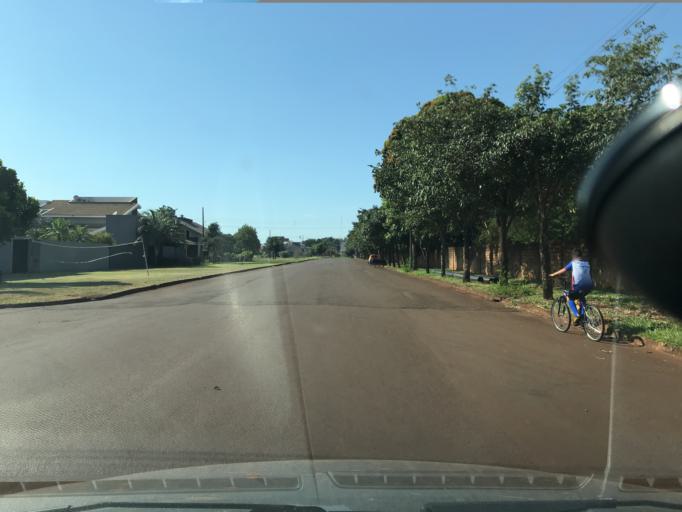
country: BR
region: Parana
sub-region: Palotina
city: Palotina
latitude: -24.2909
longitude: -53.8400
